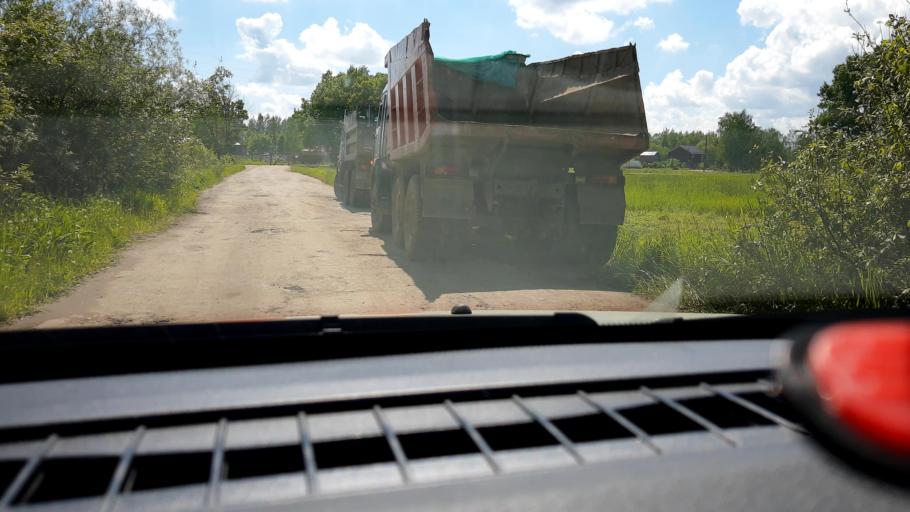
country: RU
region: Nizjnij Novgorod
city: Gorbatovka
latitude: 56.3890
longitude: 43.8118
